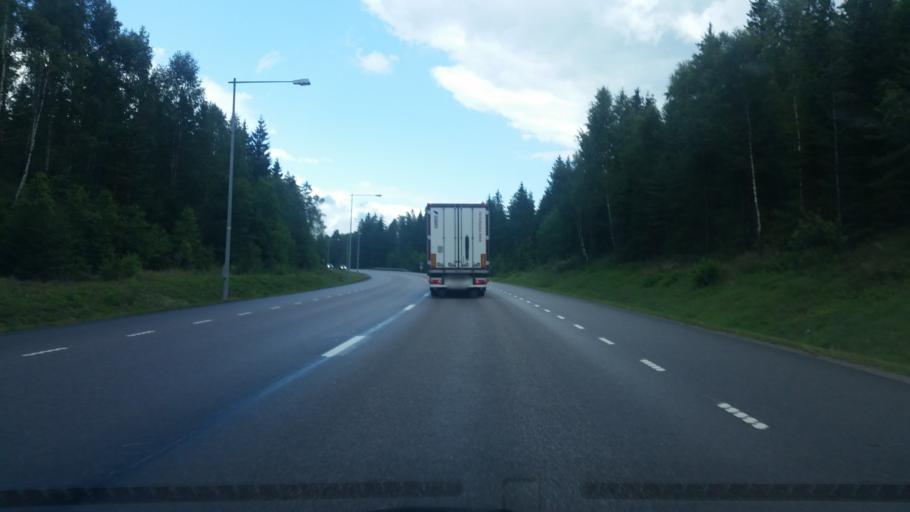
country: SE
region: Vaestra Goetaland
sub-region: Boras Kommun
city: Boras
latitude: 57.6850
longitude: 12.9405
